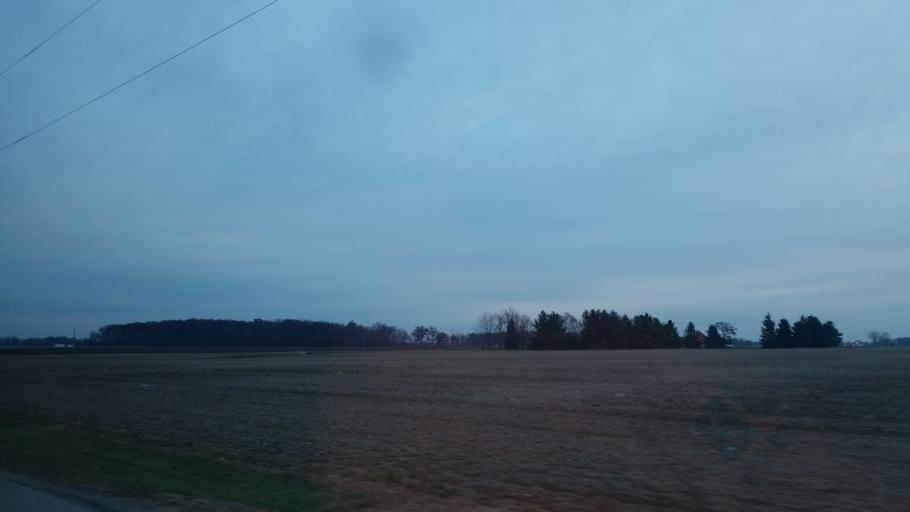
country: US
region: Indiana
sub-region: Adams County
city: Decatur
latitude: 40.7888
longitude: -84.9207
